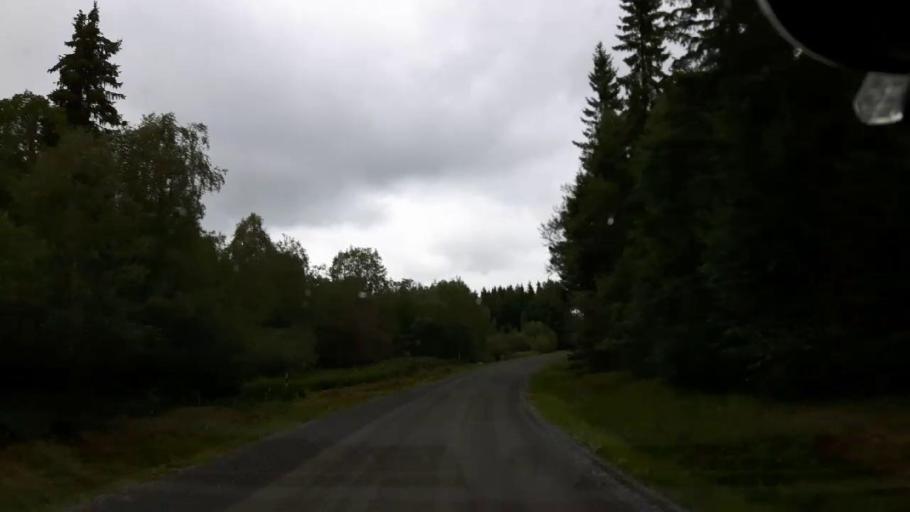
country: SE
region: Jaemtland
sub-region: OEstersunds Kommun
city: Ostersund
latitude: 63.0074
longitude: 14.5840
